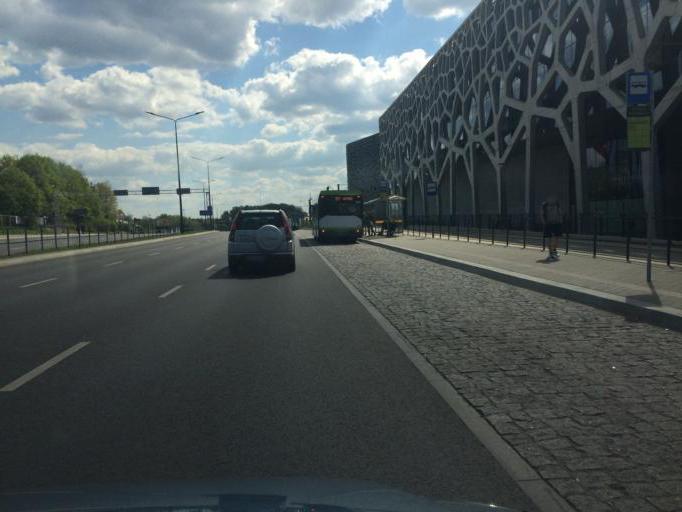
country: PL
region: Warmian-Masurian Voivodeship
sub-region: Powiat olsztynski
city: Olsztyn
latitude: 53.7551
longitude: 20.4861
